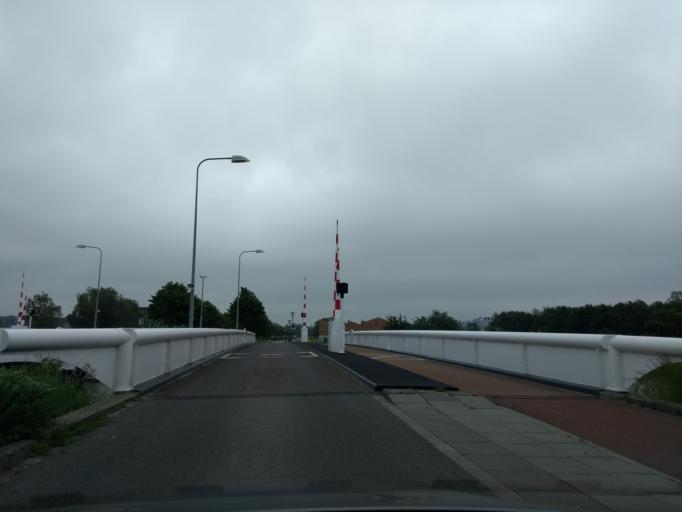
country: NL
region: Groningen
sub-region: Gemeente Groningen
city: Korrewegwijk
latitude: 53.2429
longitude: 6.5237
